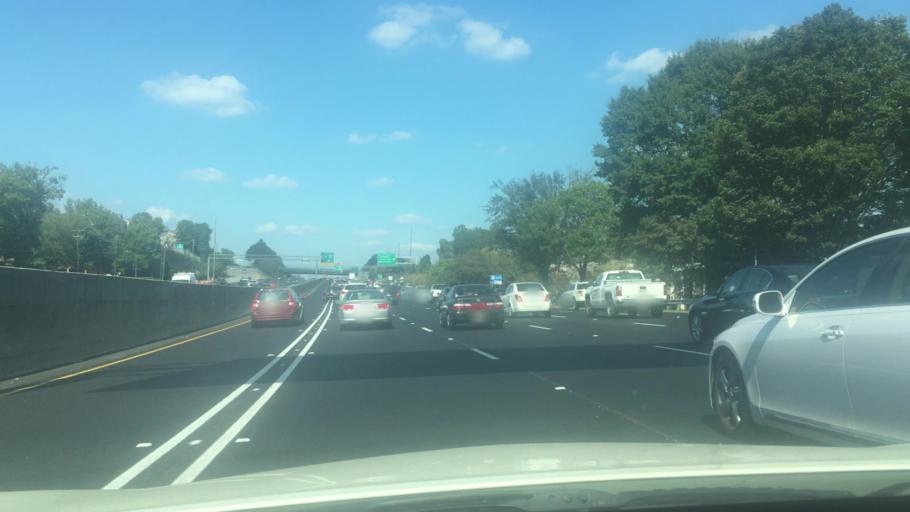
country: US
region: Georgia
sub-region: DeKalb County
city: Doraville
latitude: 33.8738
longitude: -84.2768
